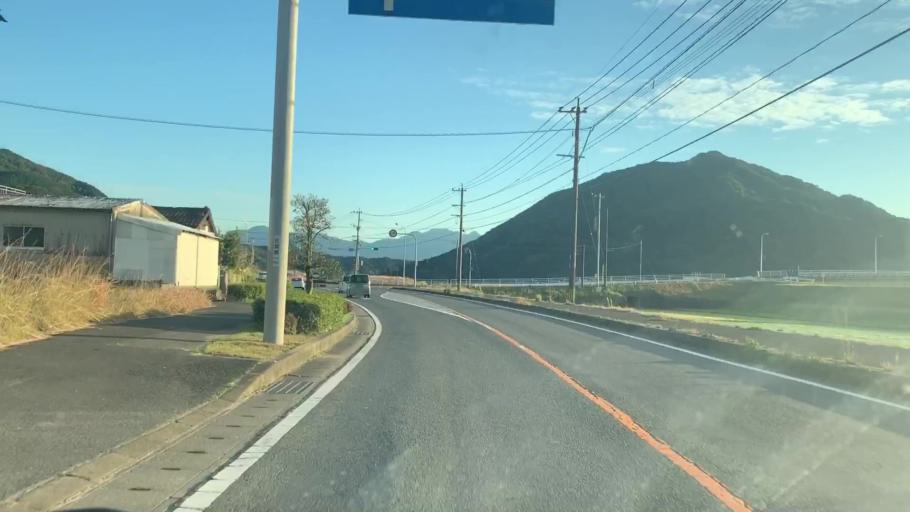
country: JP
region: Saga Prefecture
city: Karatsu
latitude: 33.3756
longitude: 130.0000
